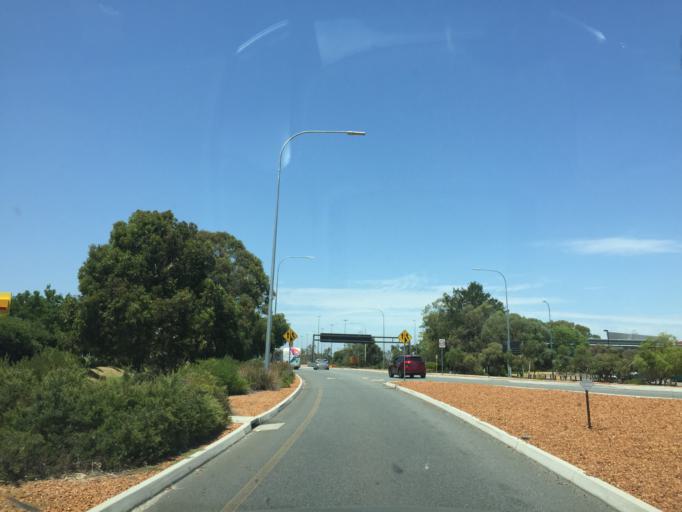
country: AU
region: Western Australia
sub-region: Belmont
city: Redcliffe
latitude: -31.9458
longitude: 115.9745
